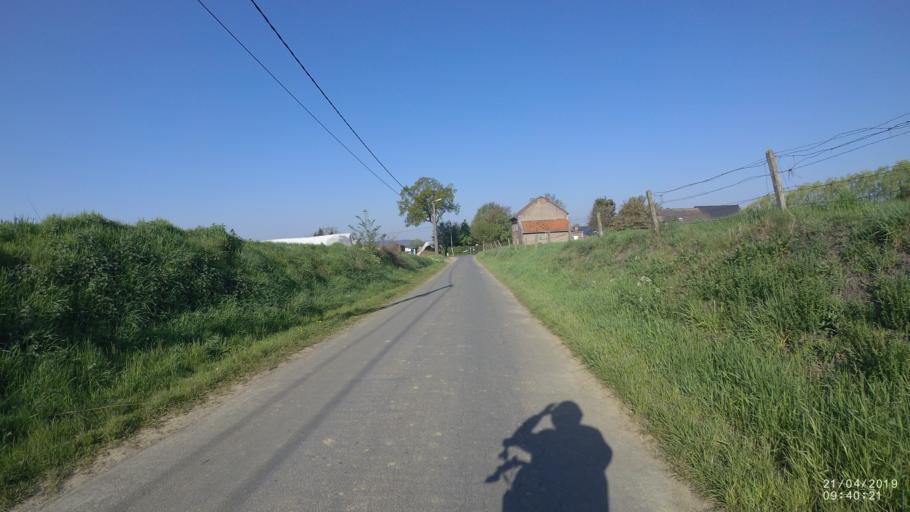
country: BE
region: Flanders
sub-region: Provincie Vlaams-Brabant
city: Lubbeek
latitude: 50.9185
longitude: 4.8209
